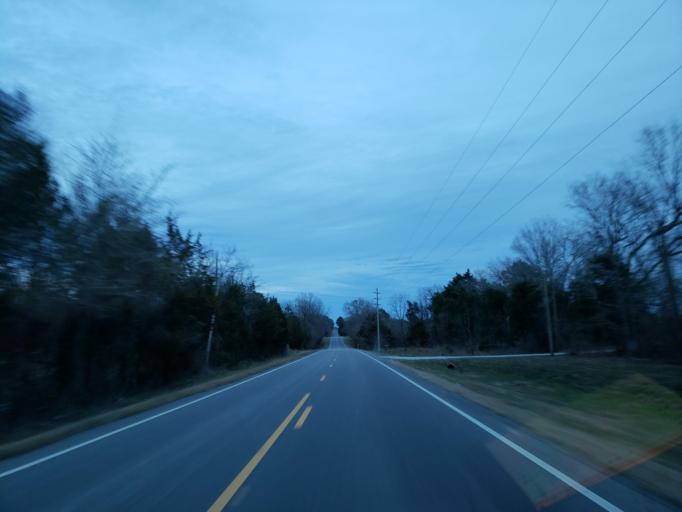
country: US
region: Alabama
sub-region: Sumter County
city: Livingston
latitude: 32.8110
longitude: -88.2647
